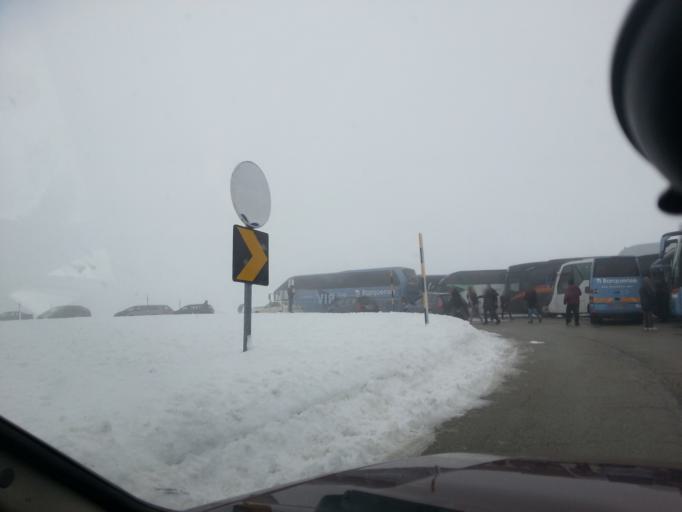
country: PT
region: Guarda
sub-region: Manteigas
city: Manteigas
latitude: 40.3218
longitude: -7.6133
